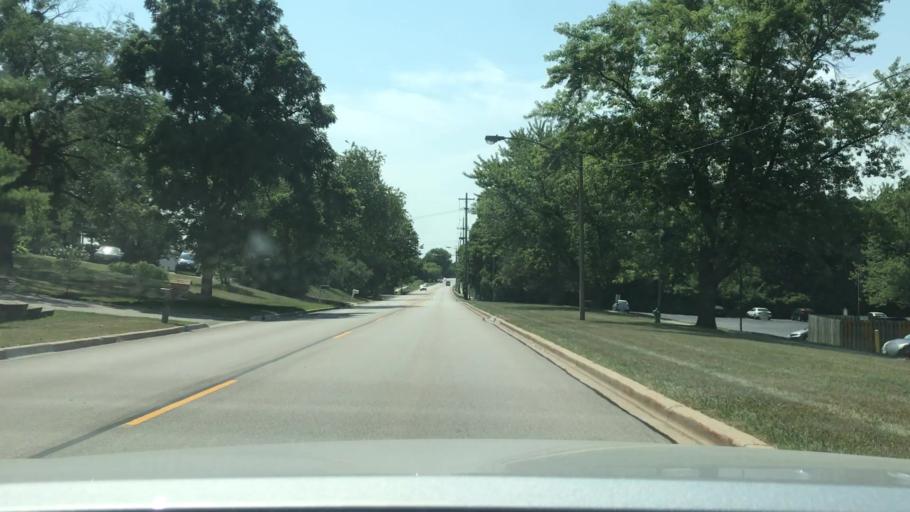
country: US
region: Illinois
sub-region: Kane County
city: Batavia
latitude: 41.8531
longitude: -88.2830
